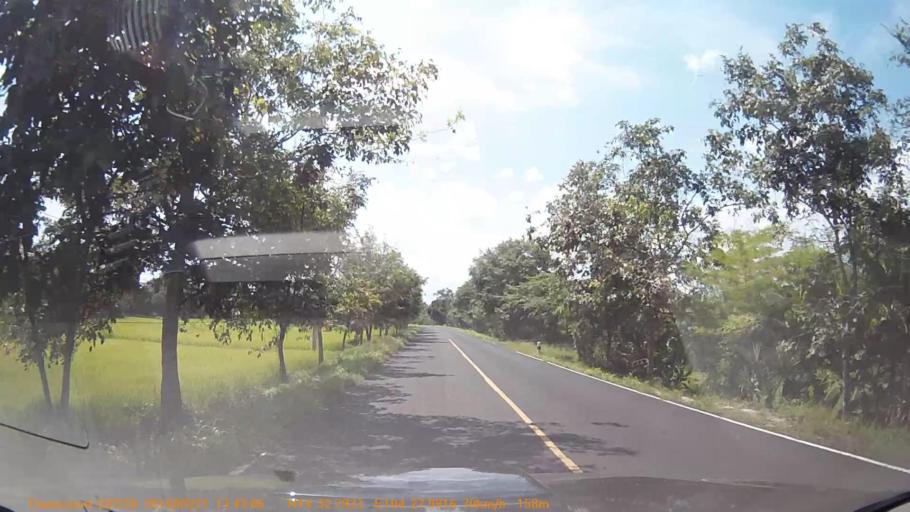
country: TH
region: Sisaket
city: Khun Han
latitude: 14.5467
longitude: 104.4660
